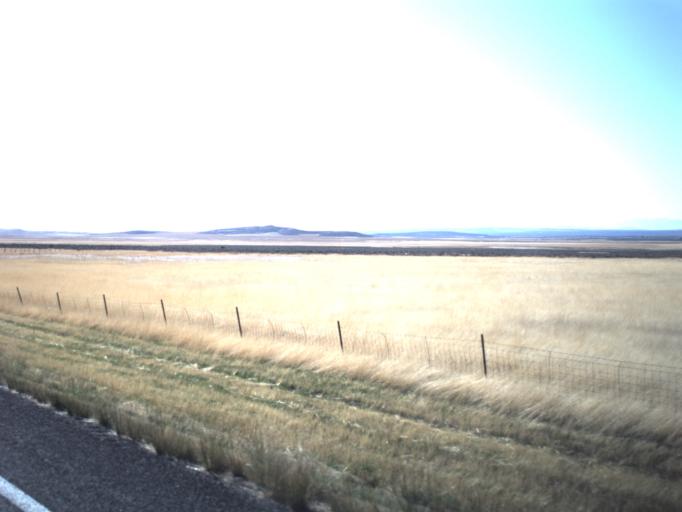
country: US
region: Utah
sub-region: Millard County
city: Fillmore
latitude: 39.0863
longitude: -112.2749
